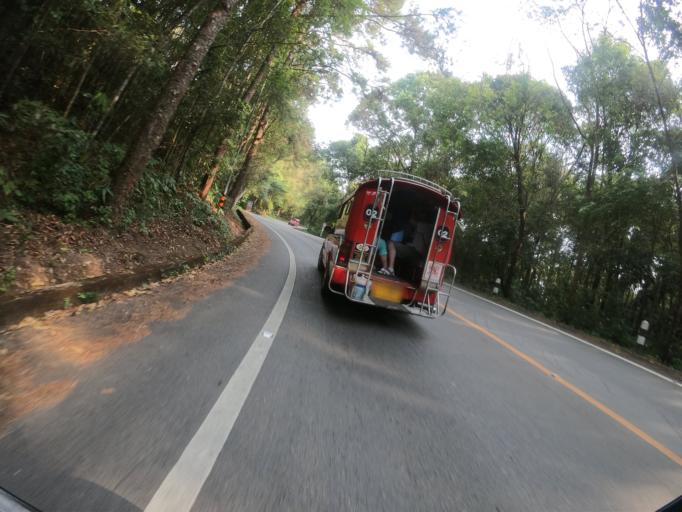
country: TH
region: Chiang Mai
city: Chiang Mai
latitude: 18.8012
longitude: 98.9060
